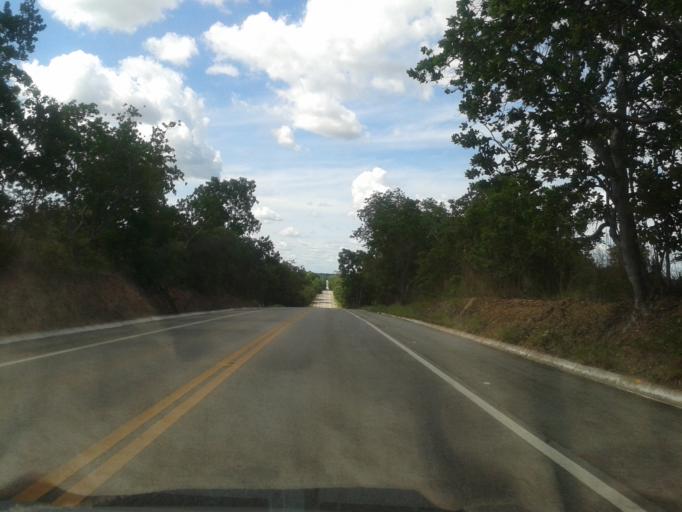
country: BR
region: Goias
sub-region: Itapuranga
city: Itapuranga
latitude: -15.5370
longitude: -50.2914
